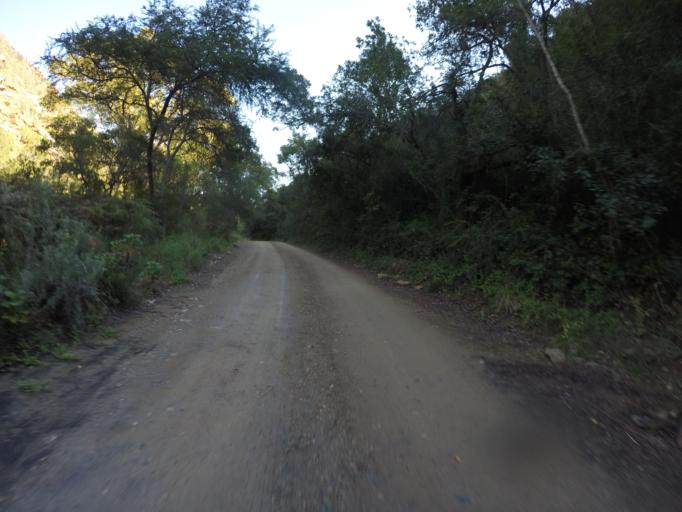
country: ZA
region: Eastern Cape
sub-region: Cacadu District Municipality
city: Kareedouw
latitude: -33.6585
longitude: 24.5330
